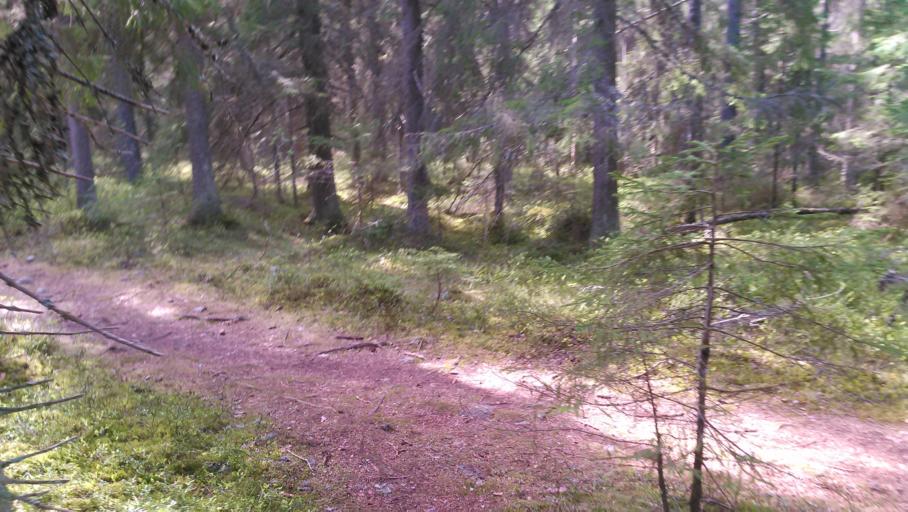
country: SE
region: Vaesterbotten
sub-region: Umea Kommun
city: Umea
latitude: 63.8392
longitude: 20.3038
